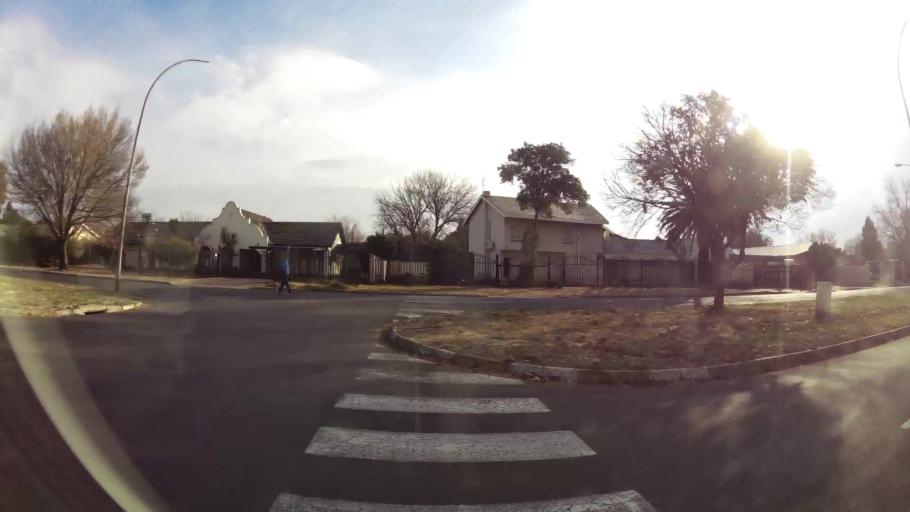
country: ZA
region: Orange Free State
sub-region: Mangaung Metropolitan Municipality
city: Bloemfontein
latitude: -29.1236
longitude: 26.1776
